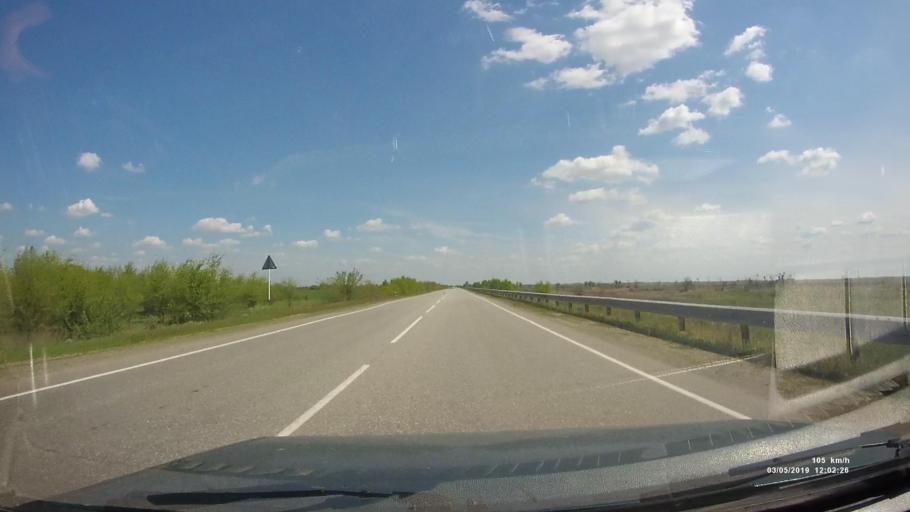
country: RU
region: Rostov
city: Bagayevskaya
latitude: 47.2719
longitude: 40.3673
